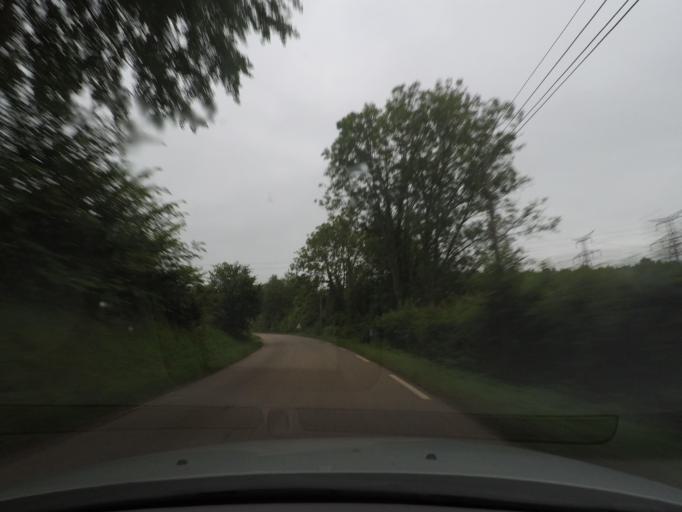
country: FR
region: Haute-Normandie
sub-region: Departement de la Seine-Maritime
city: Fontaine-le-Bourg
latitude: 49.5844
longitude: 1.2345
